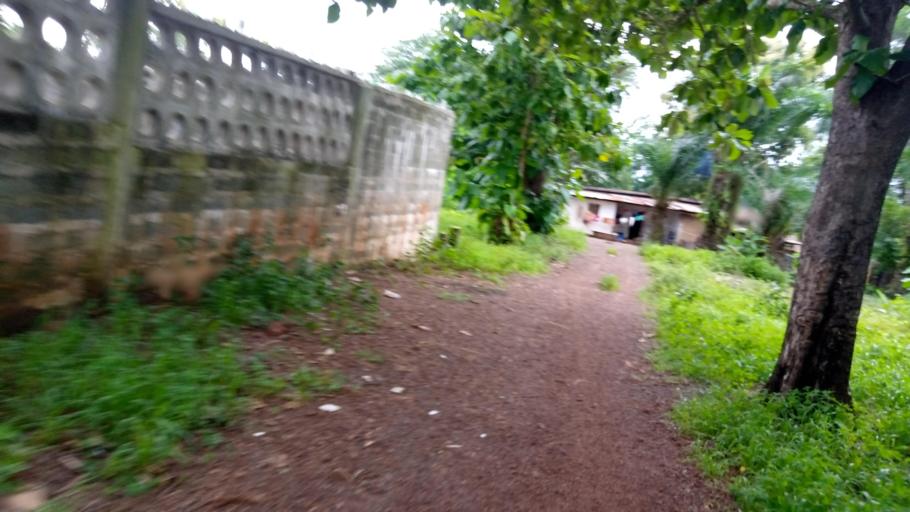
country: SL
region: Southern Province
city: Moyamba
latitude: 8.1618
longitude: -12.4417
